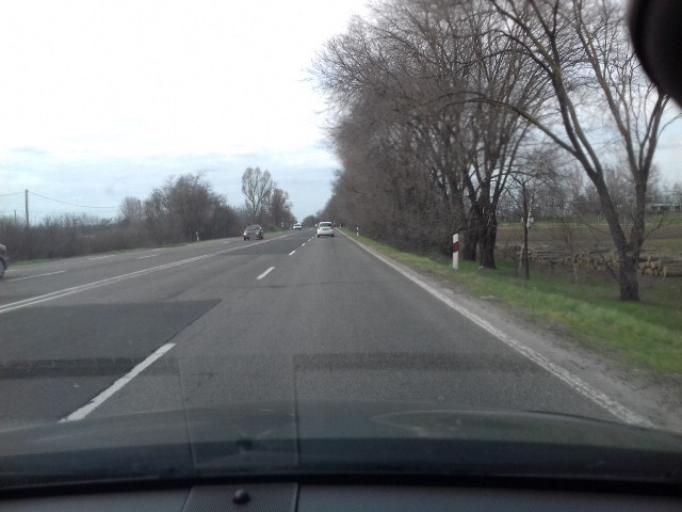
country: HU
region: Bacs-Kiskun
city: Kecskemet
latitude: 46.9687
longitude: 19.6365
